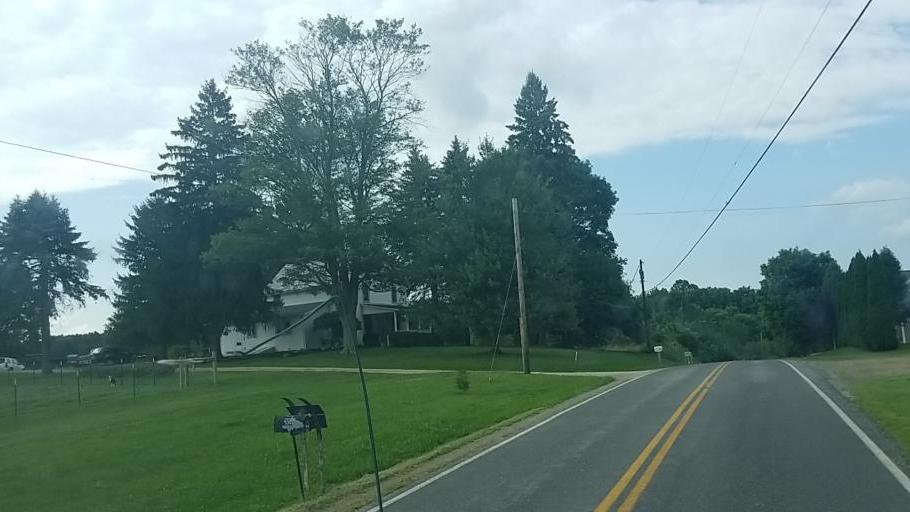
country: US
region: Ohio
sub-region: Medina County
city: Westfield Center
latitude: 41.0167
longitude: -81.9417
